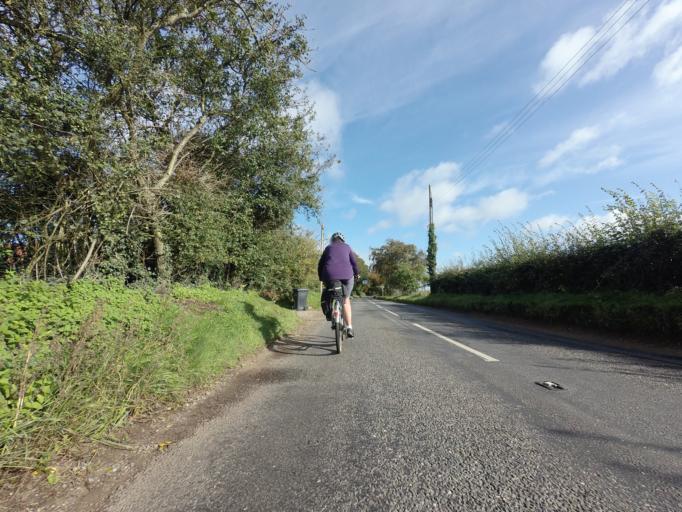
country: GB
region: England
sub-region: Norfolk
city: Wells-next-the-Sea
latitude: 52.8959
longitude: 0.6815
